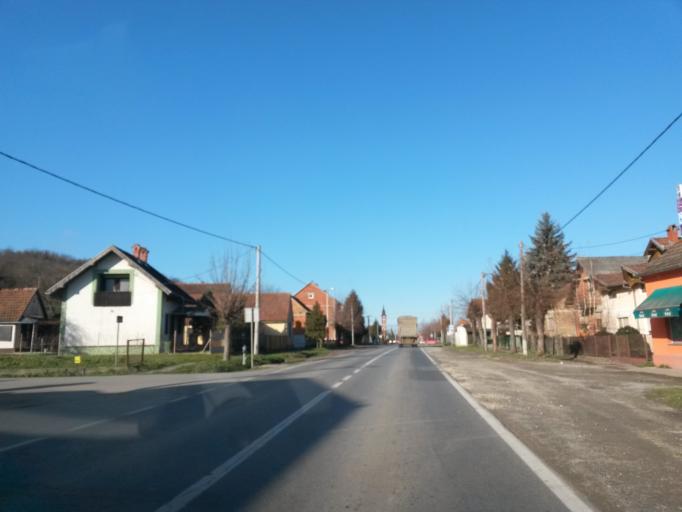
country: HR
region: Virovitick-Podravska
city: Suhopolje
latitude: 45.7573
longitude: 17.5773
